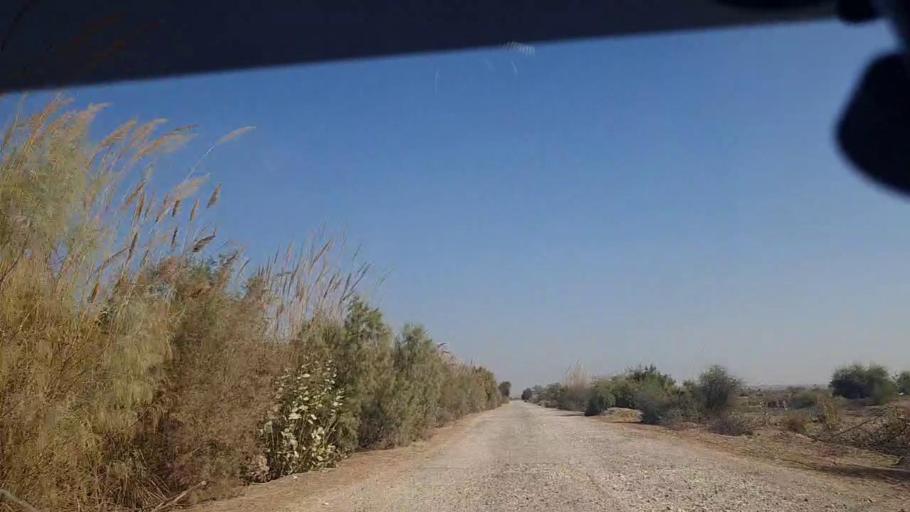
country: PK
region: Sindh
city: Khanpur
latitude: 27.5647
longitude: 69.3056
